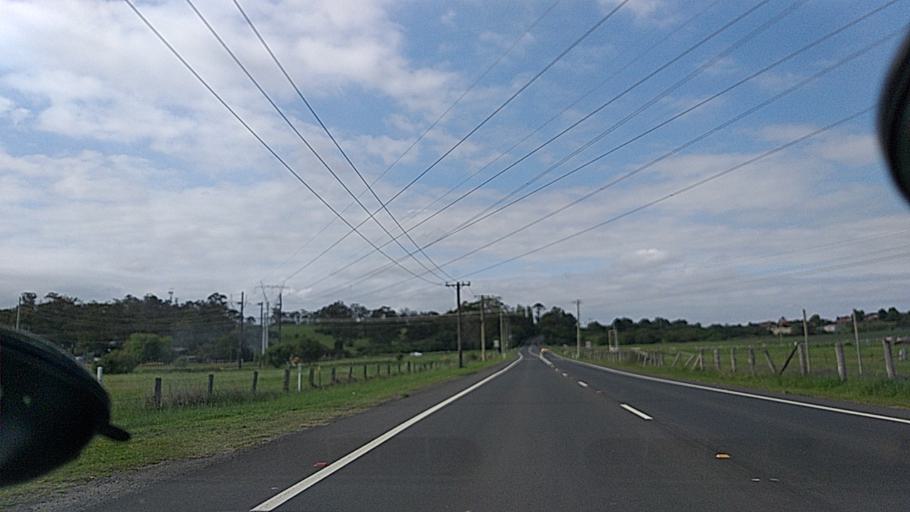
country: AU
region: New South Wales
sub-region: Campbelltown Municipality
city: Glen Alpine
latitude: -34.0953
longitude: 150.7689
